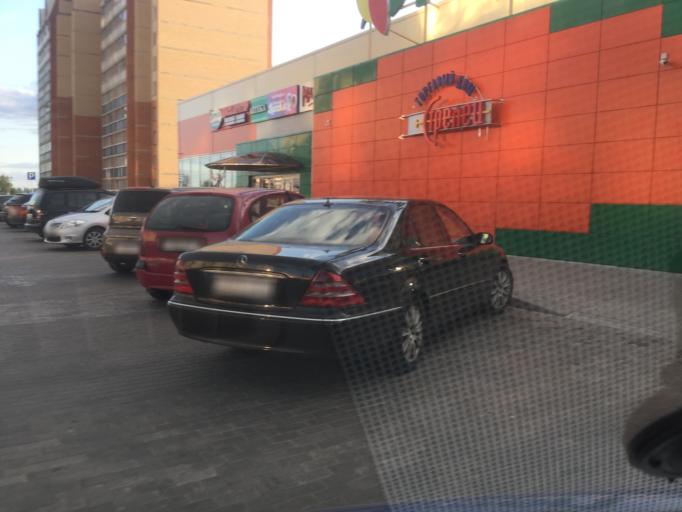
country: BY
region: Vitebsk
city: Polatsk
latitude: 55.4948
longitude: 28.7514
